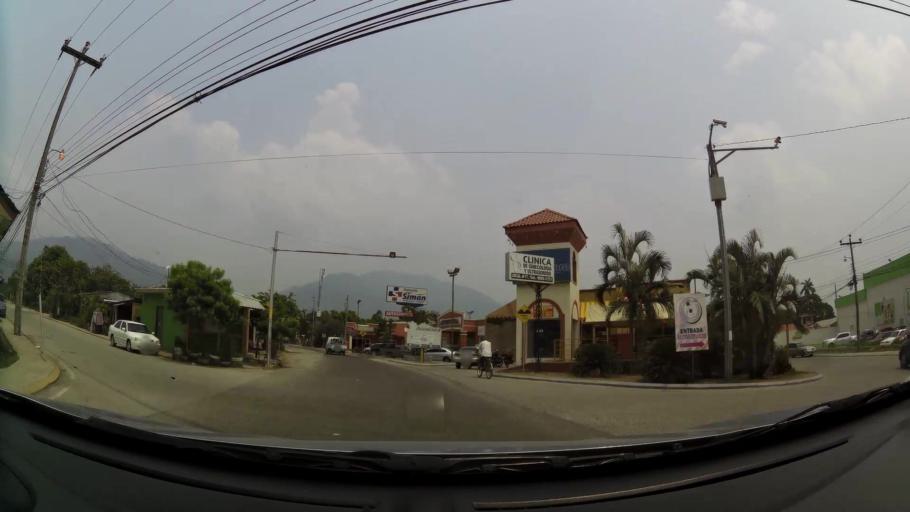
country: HN
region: Yoro
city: El Progreso
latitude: 15.3995
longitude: -87.8046
